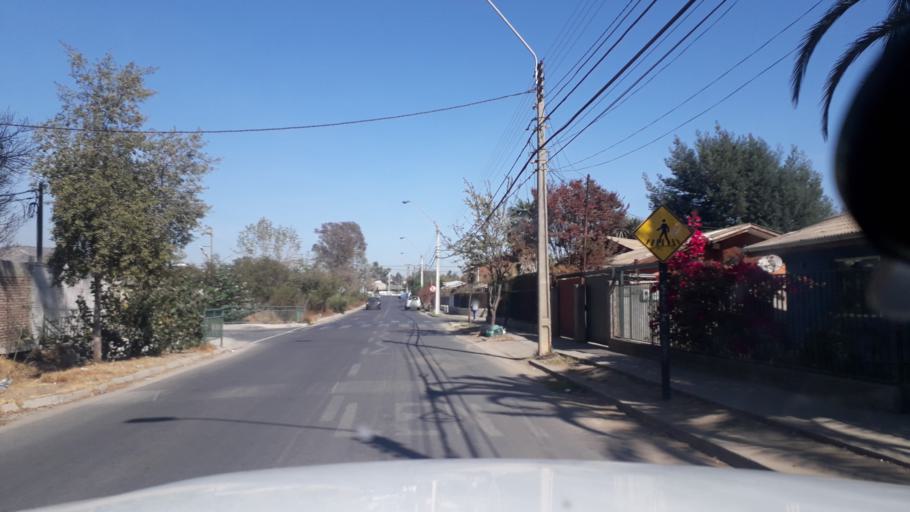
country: CL
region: Valparaiso
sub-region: Provincia de Marga Marga
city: Villa Alemana
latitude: -33.0461
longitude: -71.3494
